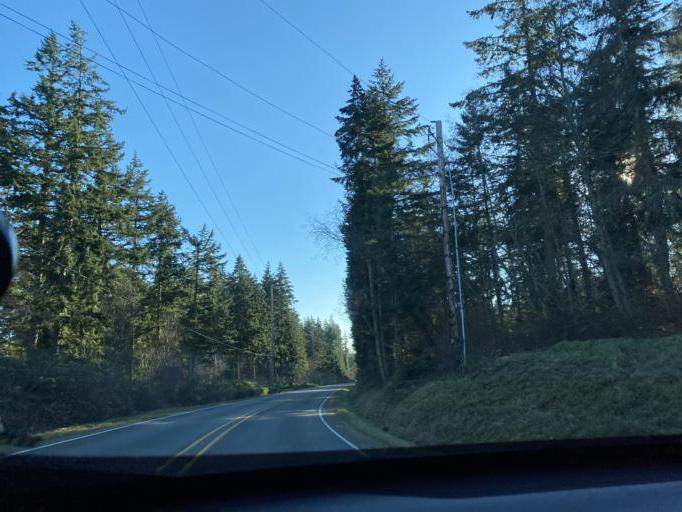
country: US
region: Washington
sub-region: Island County
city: Camano
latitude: 48.1203
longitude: -122.5617
